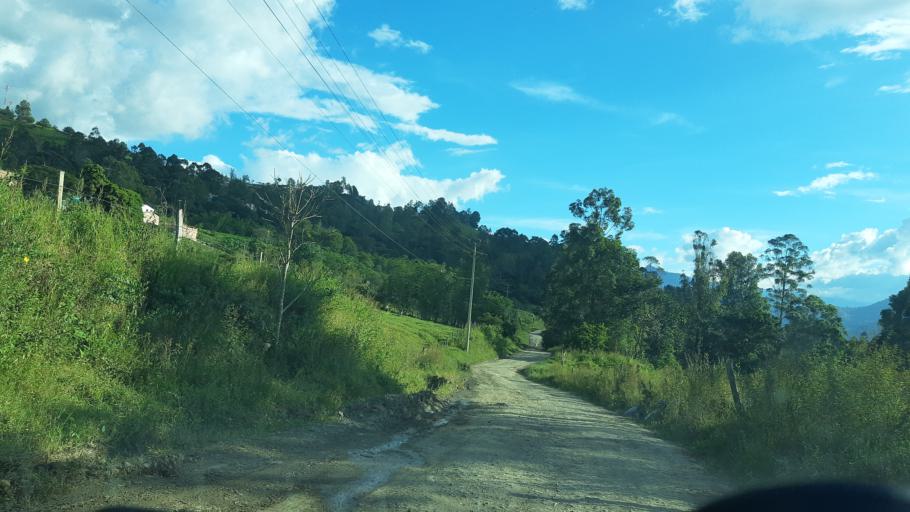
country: CO
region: Boyaca
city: Garagoa
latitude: 5.0836
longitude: -73.3707
